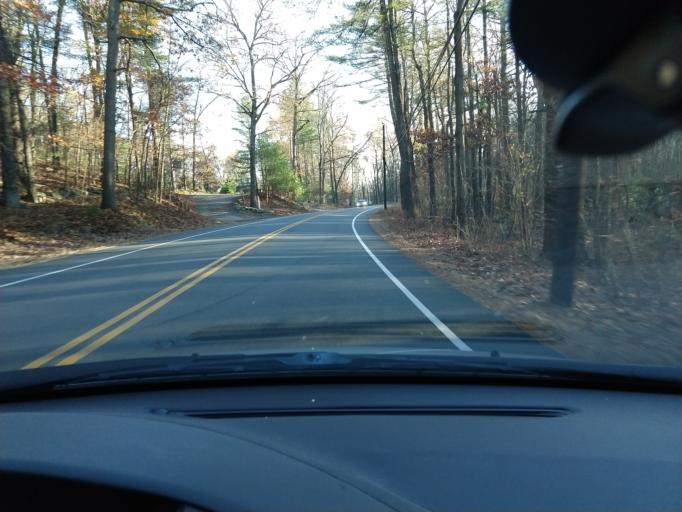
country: US
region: Massachusetts
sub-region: Middlesex County
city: Westford
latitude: 42.5450
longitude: -71.4083
